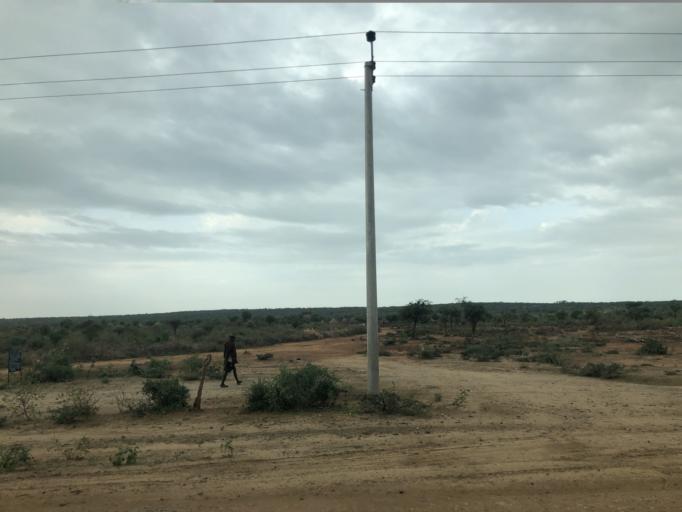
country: ET
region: Southern Nations, Nationalities, and People's Region
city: Turmi
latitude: 4.9914
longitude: 36.4736
